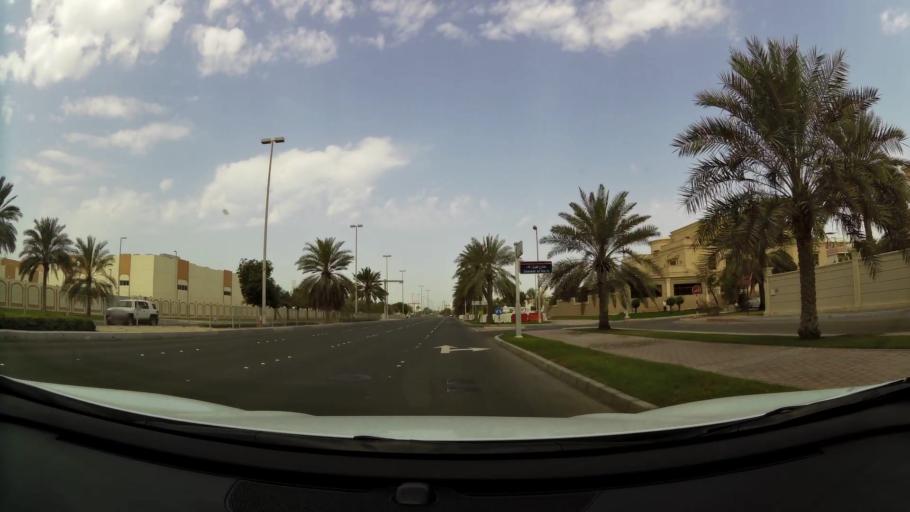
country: AE
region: Abu Dhabi
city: Abu Dhabi
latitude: 24.4491
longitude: 54.3572
